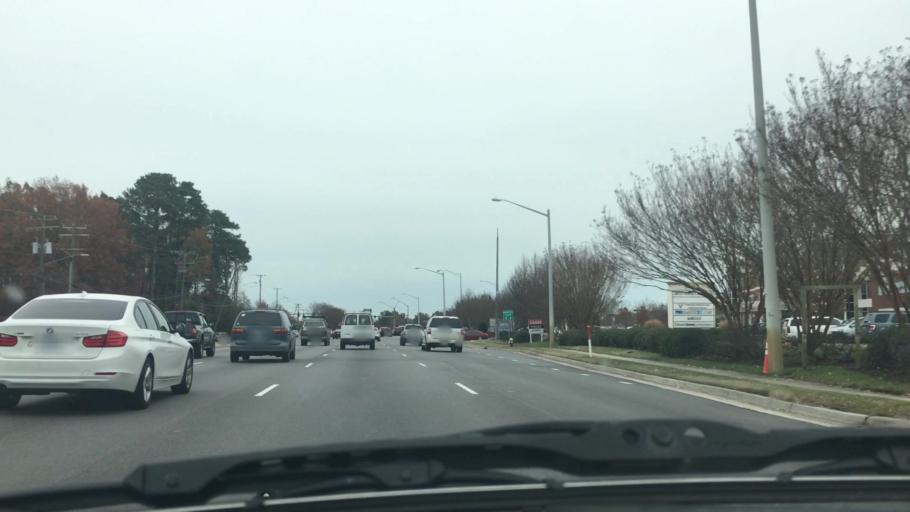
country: US
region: Virginia
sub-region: City of Chesapeake
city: Chesapeake
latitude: 36.8249
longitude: -76.1290
